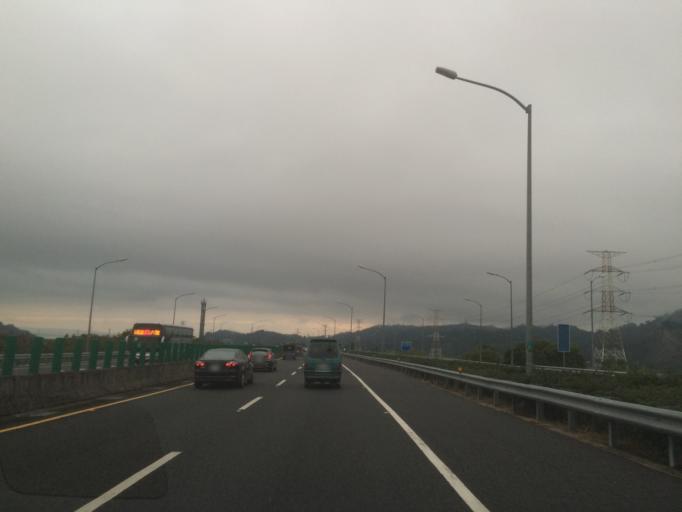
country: TW
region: Taiwan
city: Zhongxing New Village
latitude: 24.0026
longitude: 120.7365
